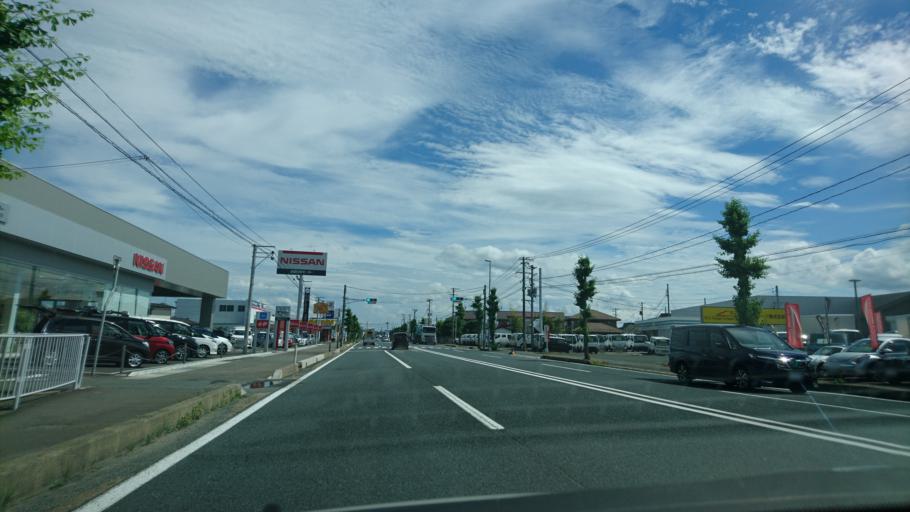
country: JP
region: Iwate
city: Morioka-shi
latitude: 39.6305
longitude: 141.1741
